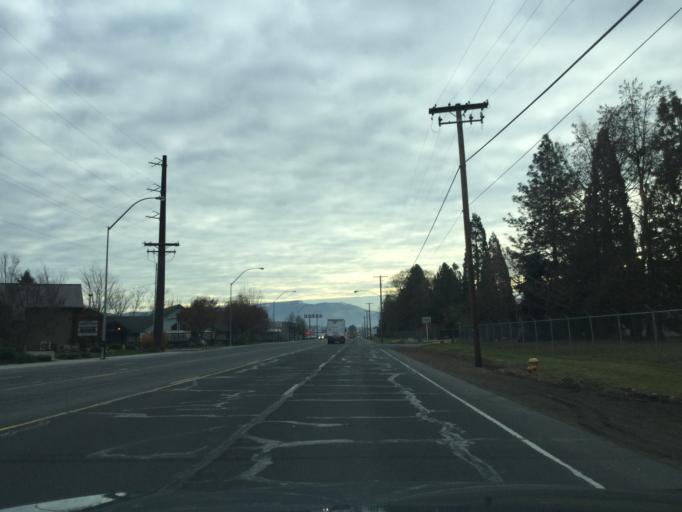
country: US
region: Oregon
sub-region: Jackson County
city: Medford
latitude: 42.3498
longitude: -122.8926
